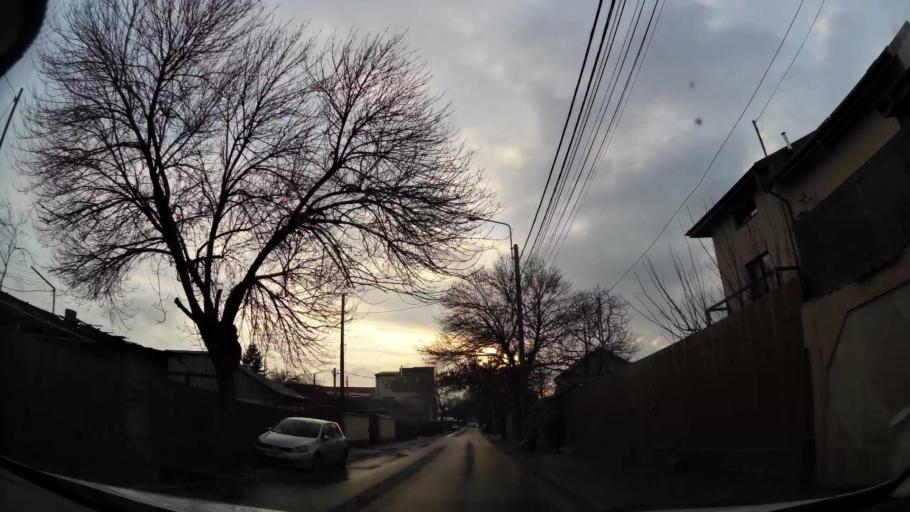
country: RO
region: Ilfov
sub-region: Voluntari City
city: Voluntari
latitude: 44.4756
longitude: 26.1681
